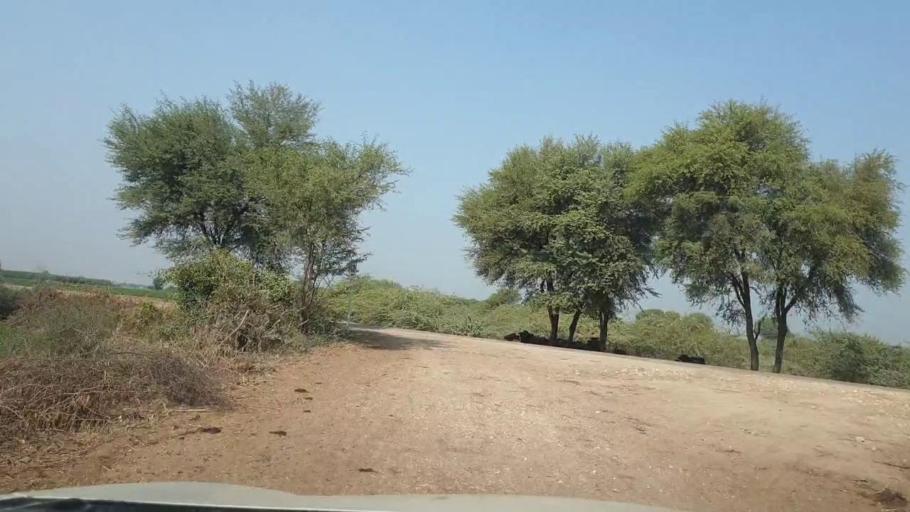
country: PK
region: Sindh
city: Bhit Shah
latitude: 25.7517
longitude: 68.4534
